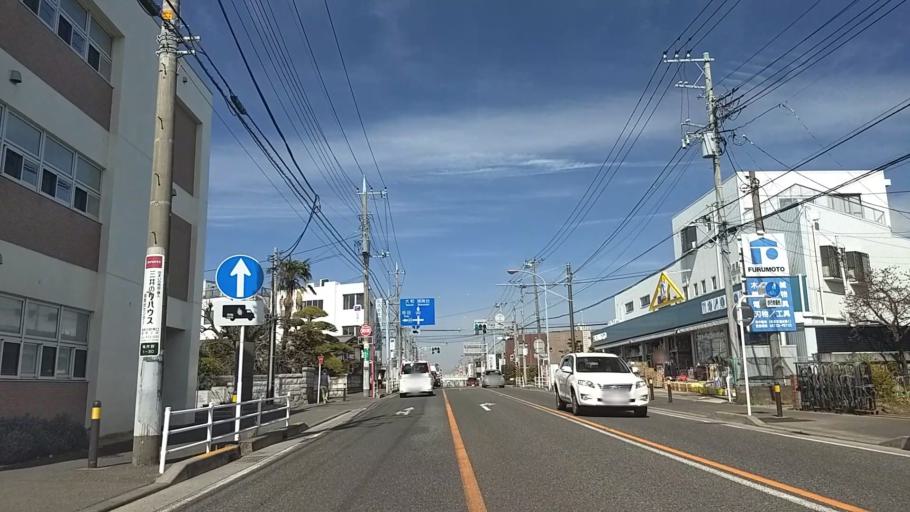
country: JP
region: Kanagawa
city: Fujisawa
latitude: 35.3863
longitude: 139.4739
